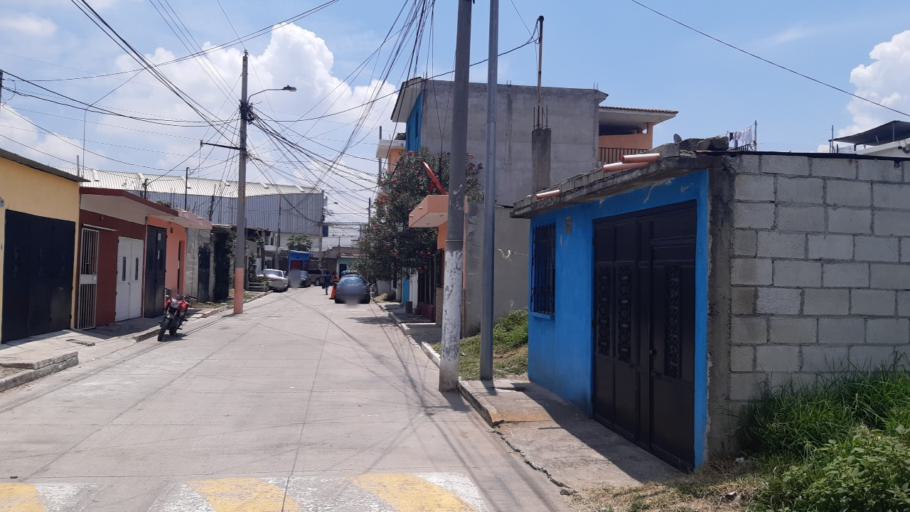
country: GT
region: Guatemala
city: Petapa
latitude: 14.5118
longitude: -90.5592
